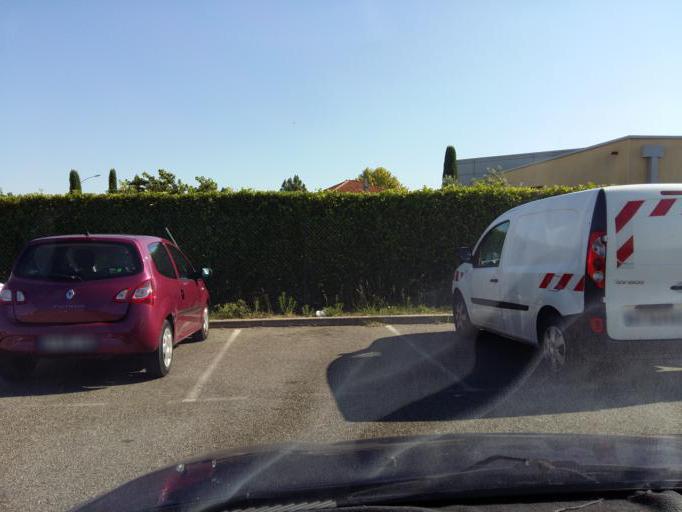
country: FR
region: Provence-Alpes-Cote d'Azur
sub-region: Departement du Vaucluse
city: Valreas
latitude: 44.3776
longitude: 4.9818
